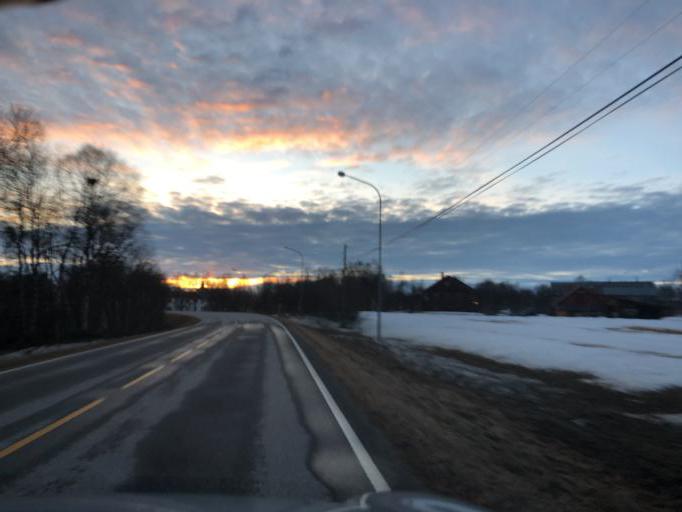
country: NO
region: Sor-Trondelag
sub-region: Tydal
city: Aas
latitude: 62.6459
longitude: 11.8774
